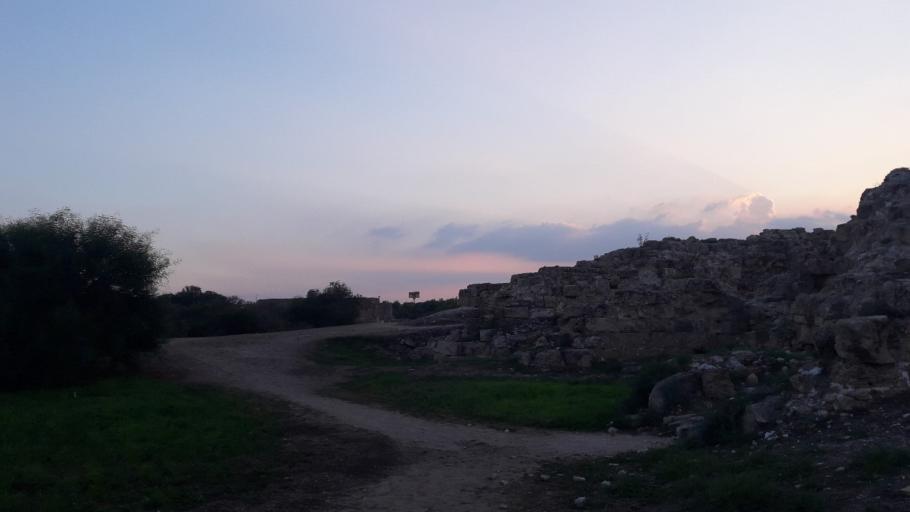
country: CY
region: Ammochostos
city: Famagusta
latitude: 35.1863
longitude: 33.9040
